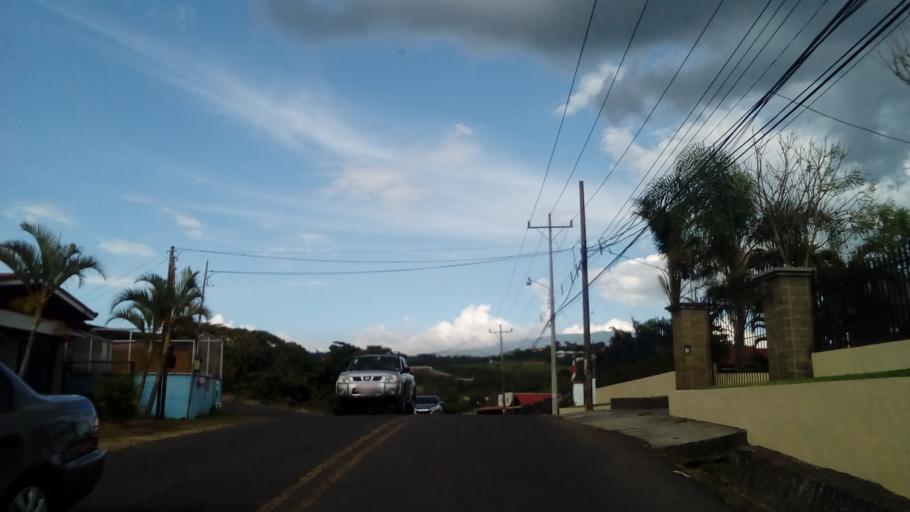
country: CR
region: Alajuela
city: Sabanilla
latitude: 10.0879
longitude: -84.2593
